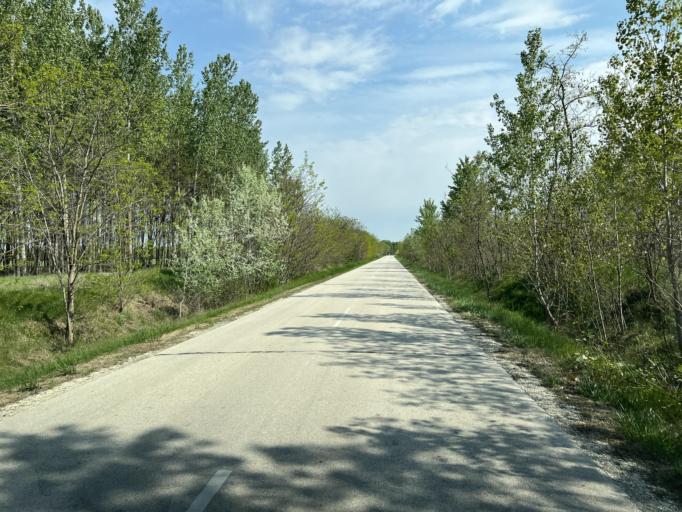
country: HU
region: Pest
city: Kocser
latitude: 47.0472
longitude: 19.9442
